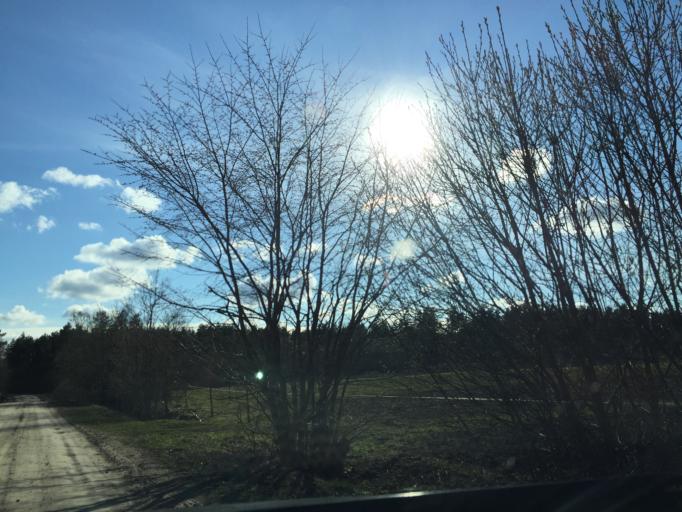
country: LV
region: Kekava
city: Kekava
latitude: 56.8508
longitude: 24.1851
